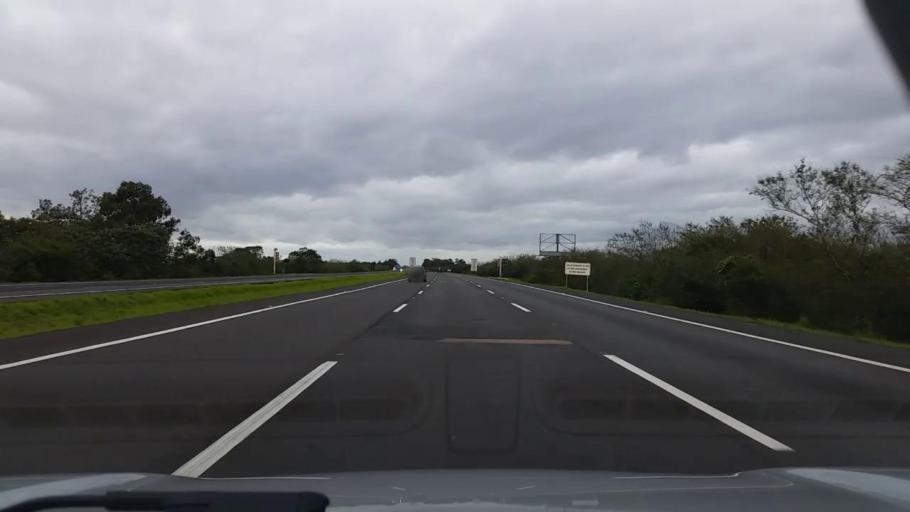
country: BR
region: Rio Grande do Sul
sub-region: Rolante
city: Rolante
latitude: -29.8839
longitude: -50.5639
